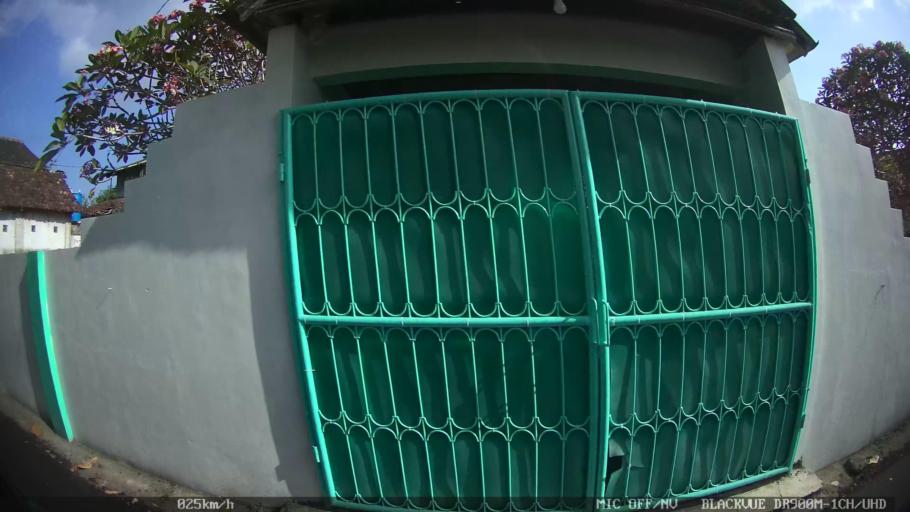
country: ID
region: Daerah Istimewa Yogyakarta
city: Yogyakarta
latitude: -7.7846
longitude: 110.3517
